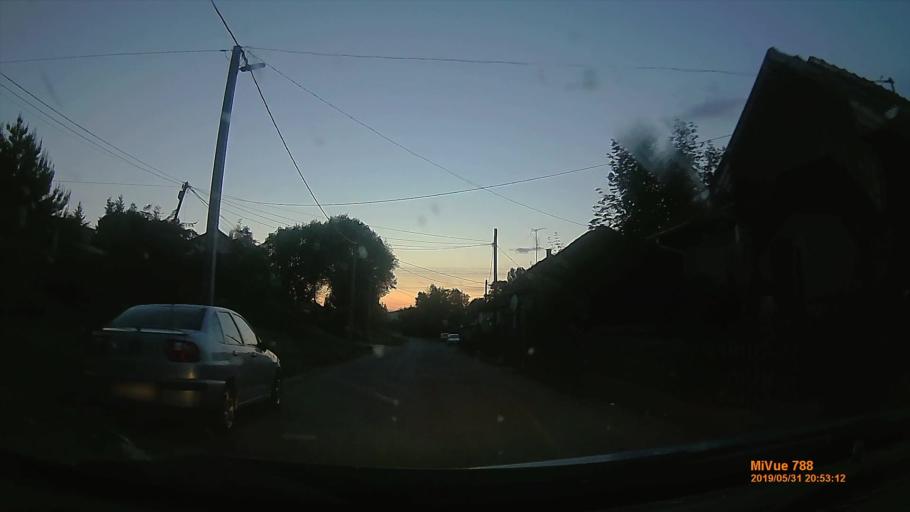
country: HU
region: Nograd
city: Nagyoroszi
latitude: 48.0483
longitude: 19.0514
